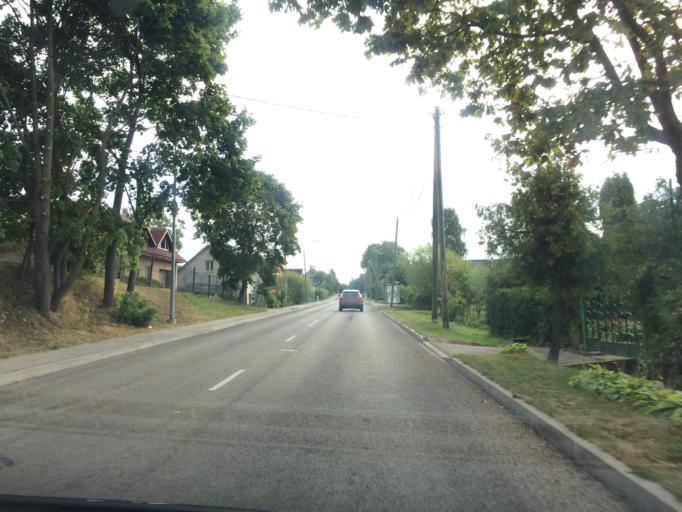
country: LV
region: Rezekne
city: Rezekne
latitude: 56.4921
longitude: 27.3335
